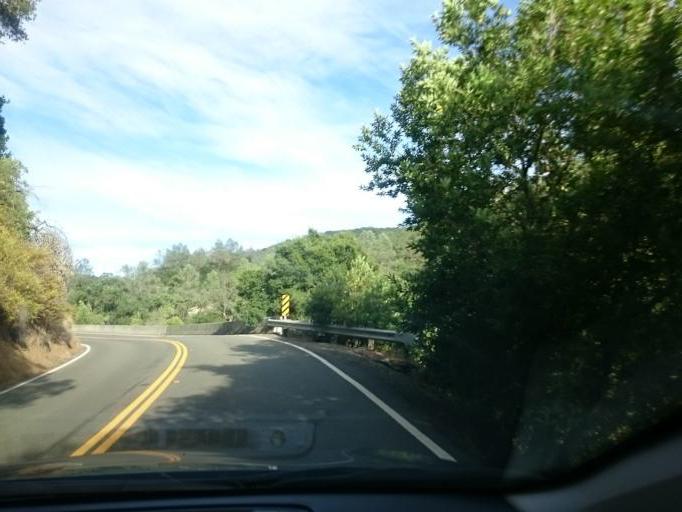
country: US
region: California
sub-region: Napa County
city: Yountville
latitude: 38.4900
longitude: -122.3291
